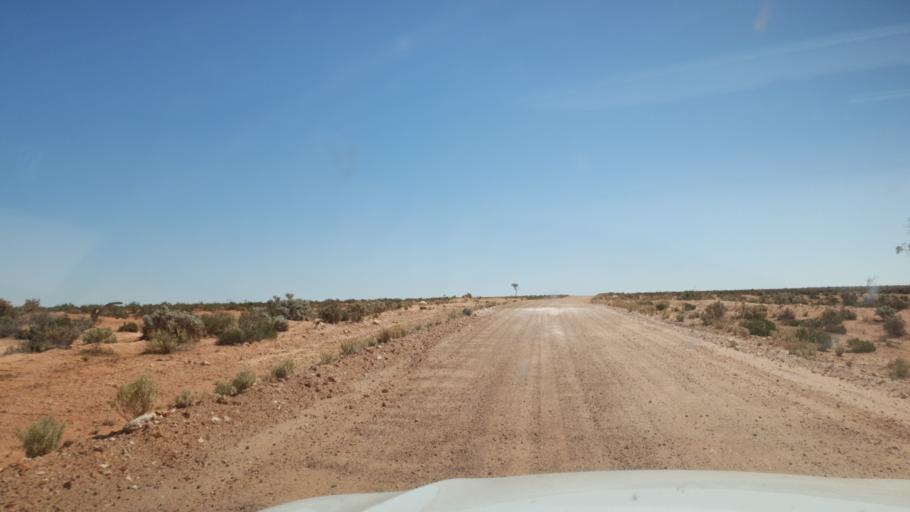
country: AU
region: South Australia
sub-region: Whyalla
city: Whyalla
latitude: -32.6469
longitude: 136.9580
